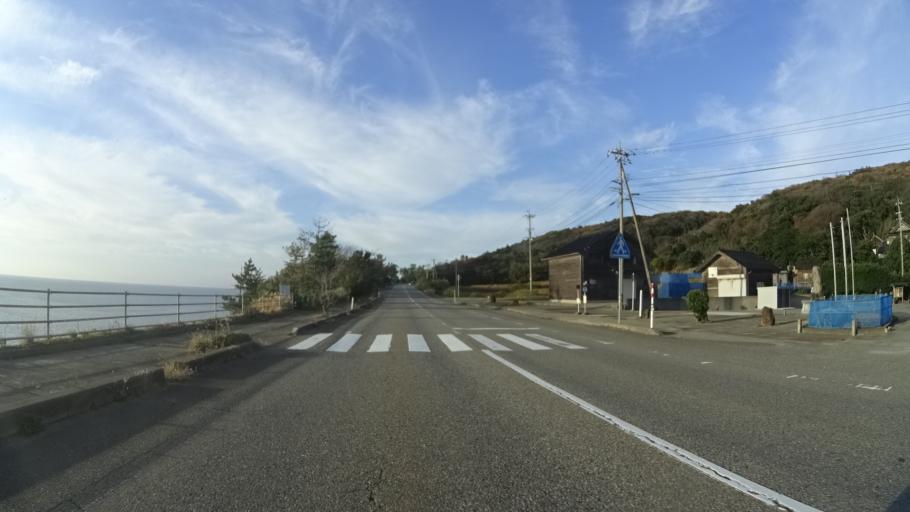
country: JP
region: Ishikawa
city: Hakui
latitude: 37.1043
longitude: 136.7301
